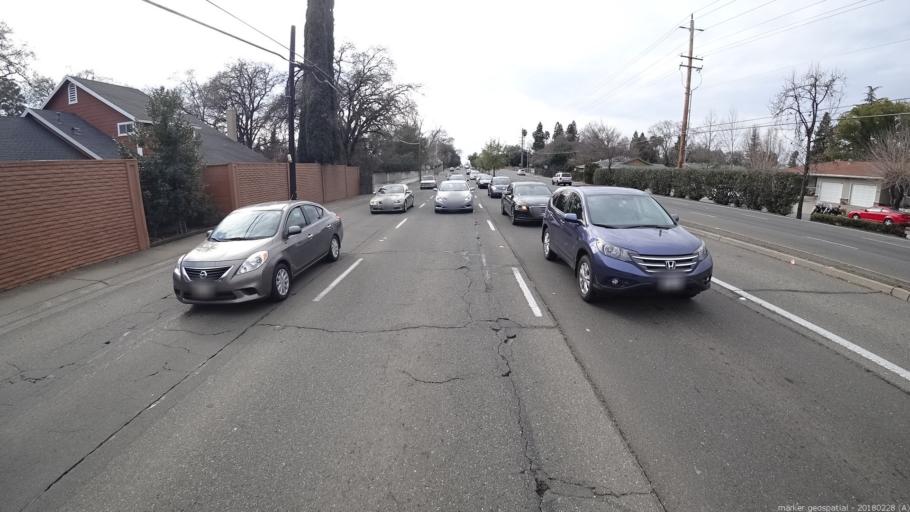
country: US
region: California
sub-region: Sacramento County
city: Fair Oaks
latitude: 38.6636
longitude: -121.2966
